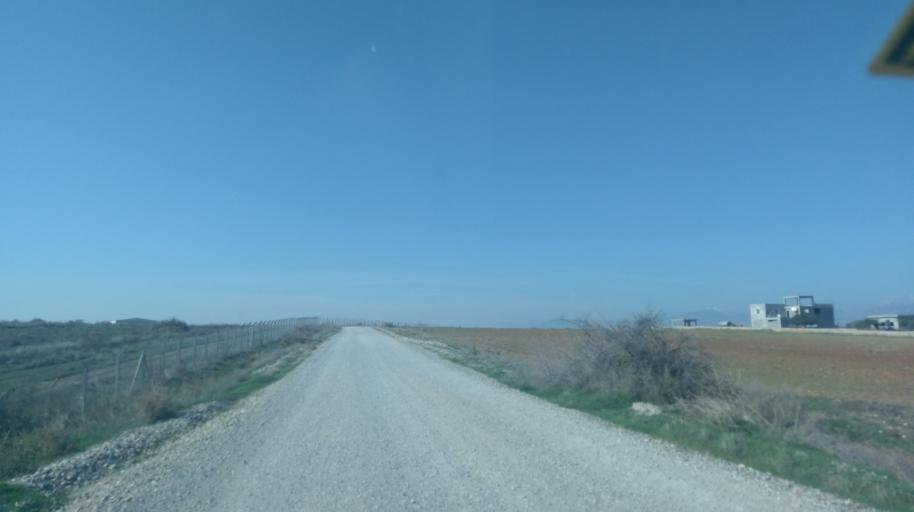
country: CY
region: Lefkosia
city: Geri
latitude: 35.1633
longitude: 33.4909
